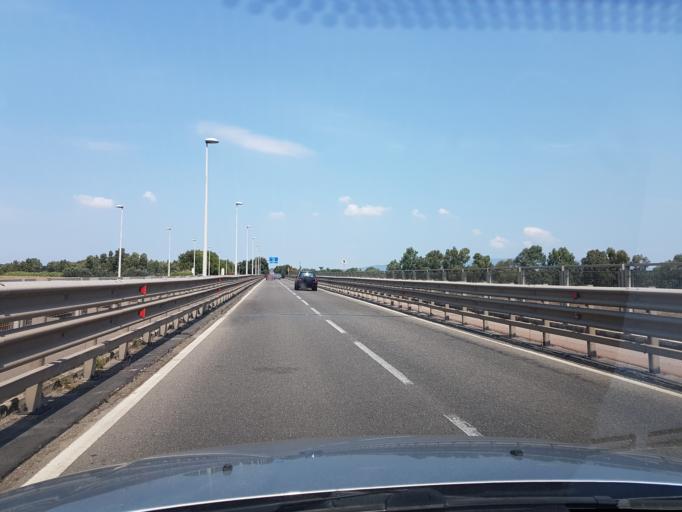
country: IT
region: Sardinia
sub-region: Provincia di Oristano
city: Donigala Fenugheddu
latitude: 39.9207
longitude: 8.5823
